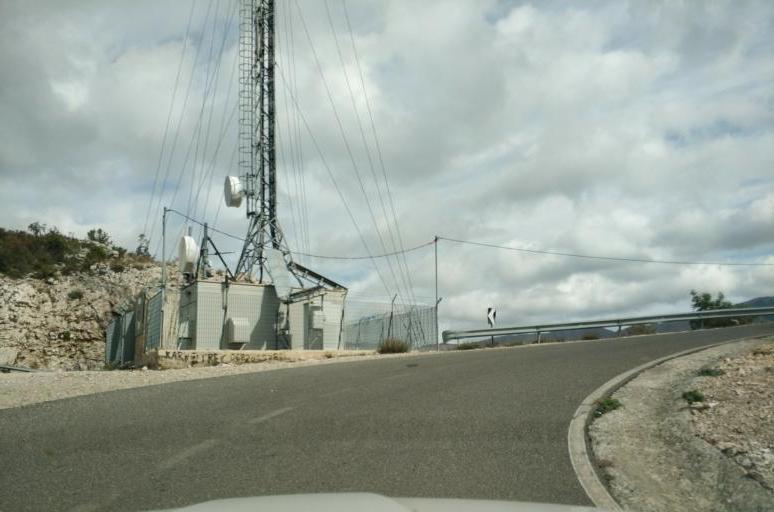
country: AL
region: Durres
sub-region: Rrethi i Krujes
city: Kruje
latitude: 41.5252
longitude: 19.8082
